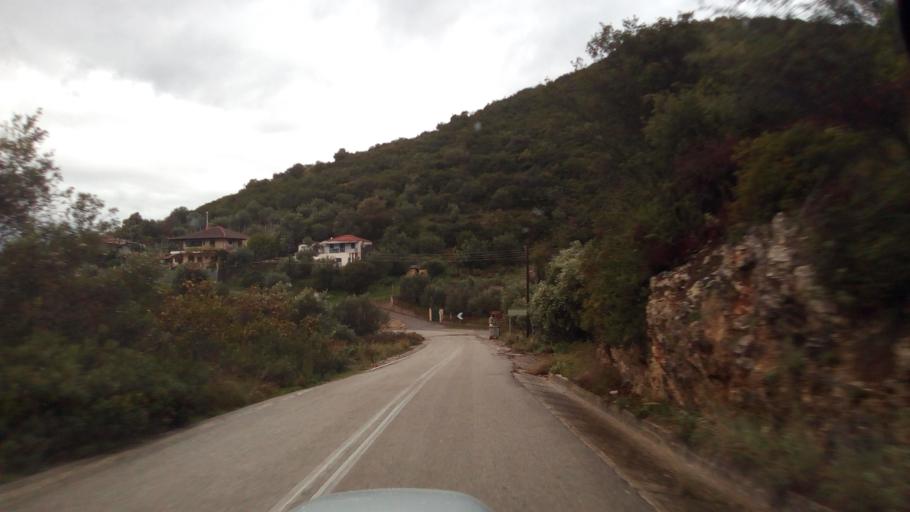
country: GR
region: West Greece
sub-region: Nomos Aitolias kai Akarnanias
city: Nafpaktos
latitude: 38.4264
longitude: 21.9314
